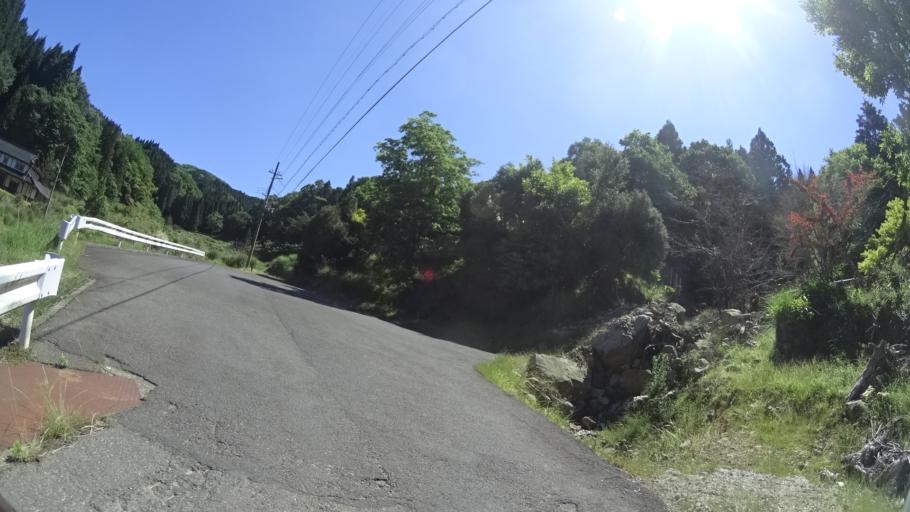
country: JP
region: Kyoto
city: Fukuchiyama
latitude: 35.3814
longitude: 135.0342
